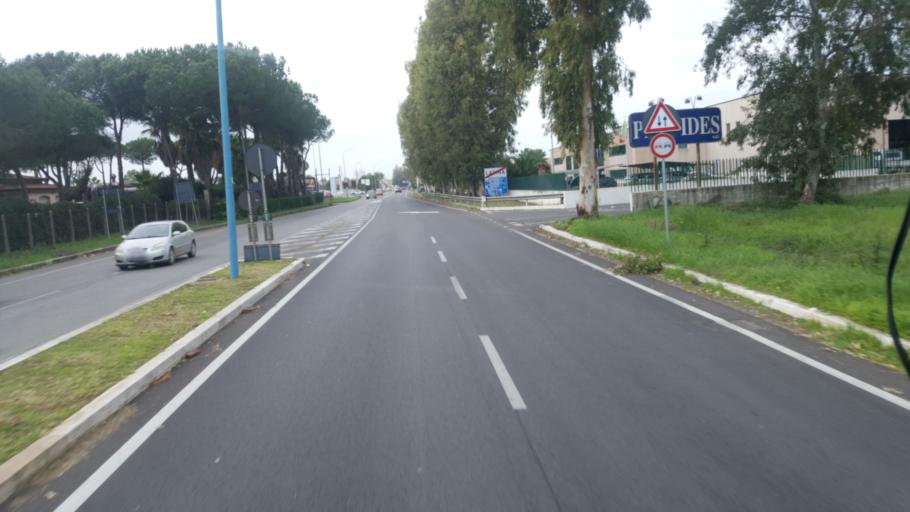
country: IT
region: Latium
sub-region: Provincia di Latina
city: Latina
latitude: 41.4791
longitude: 12.8715
